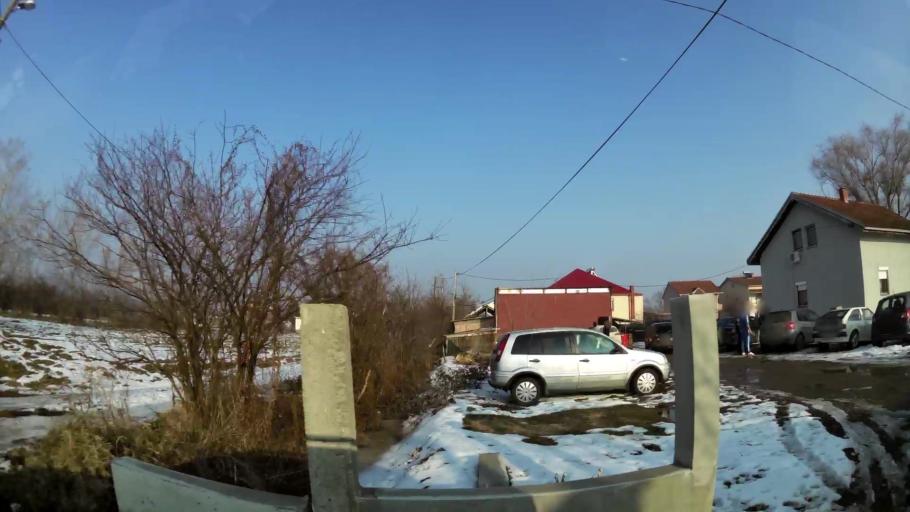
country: MK
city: Kadino
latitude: 41.9644
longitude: 21.5944
